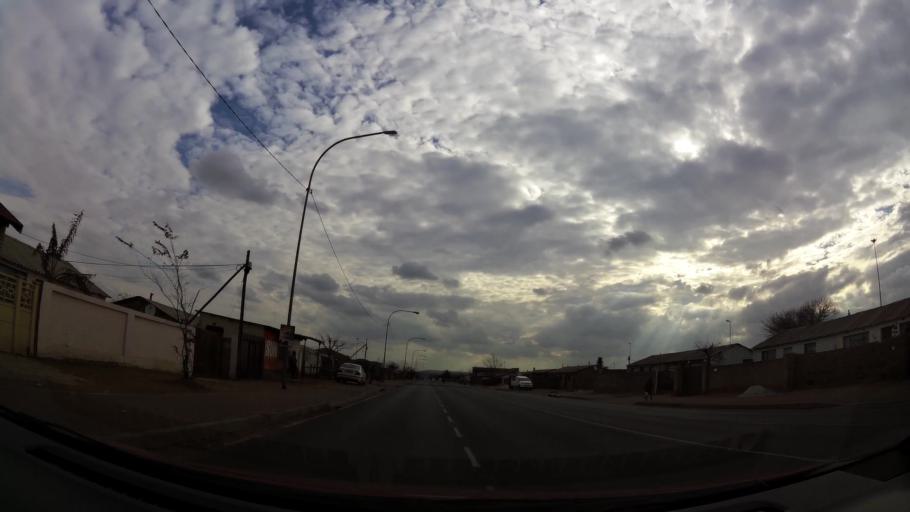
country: ZA
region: Gauteng
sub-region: City of Johannesburg Metropolitan Municipality
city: Soweto
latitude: -26.2487
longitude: 27.8282
